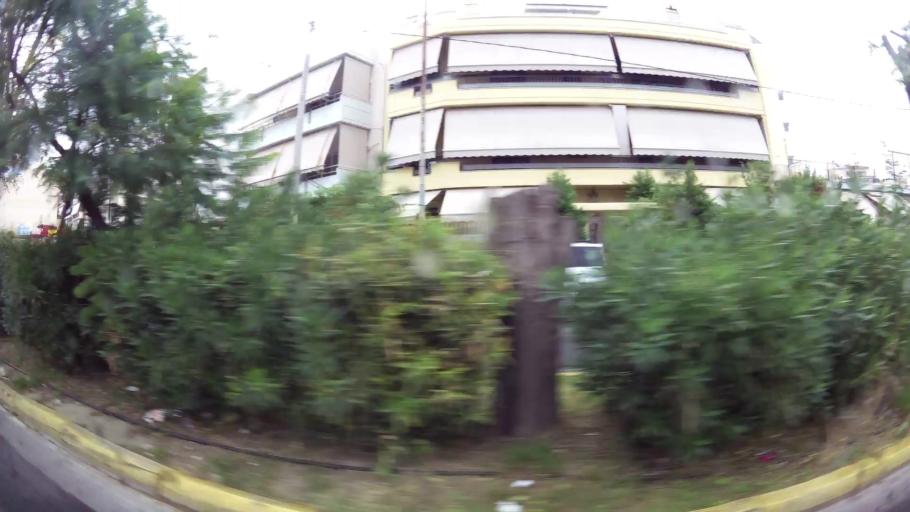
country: GR
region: Attica
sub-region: Nomos Piraios
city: Korydallos
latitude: 37.9836
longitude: 23.6418
